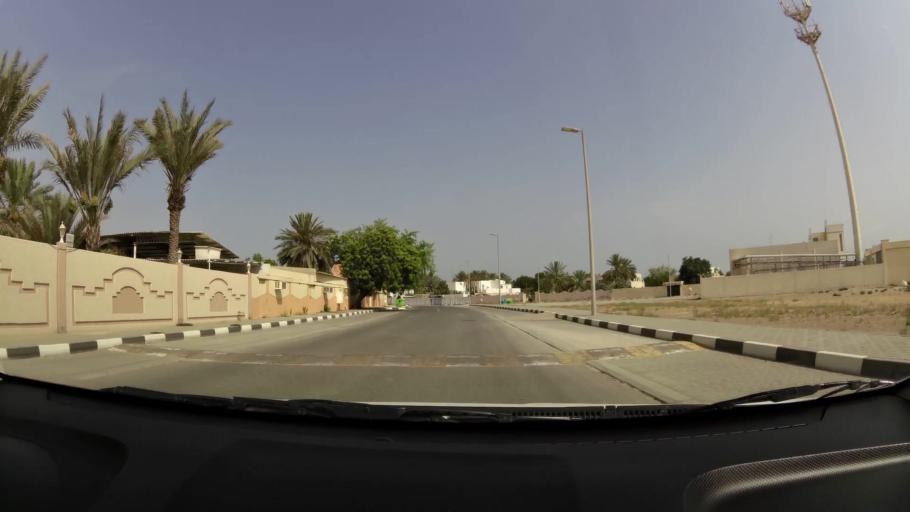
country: AE
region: Ash Shariqah
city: Sharjah
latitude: 25.3514
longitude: 55.4172
